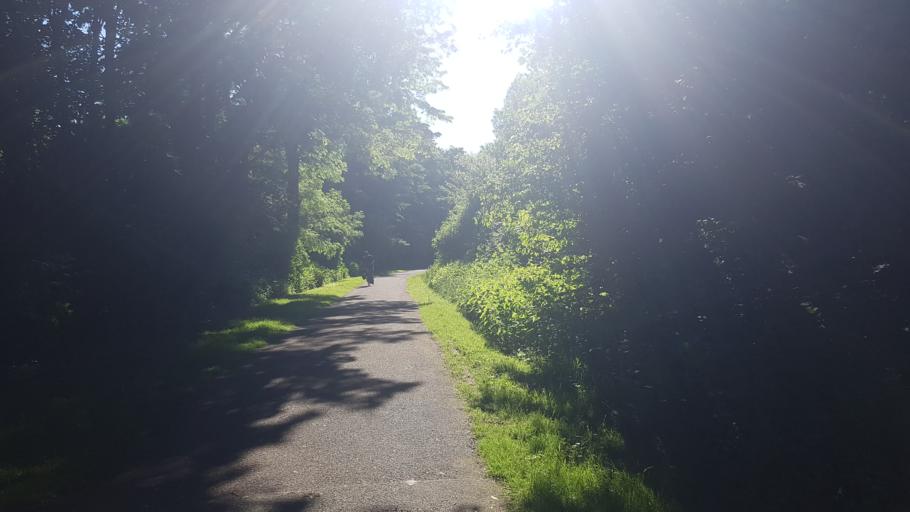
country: DE
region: North Rhine-Westphalia
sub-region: Regierungsbezirk Dusseldorf
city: Essen
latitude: 51.4682
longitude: 7.0581
